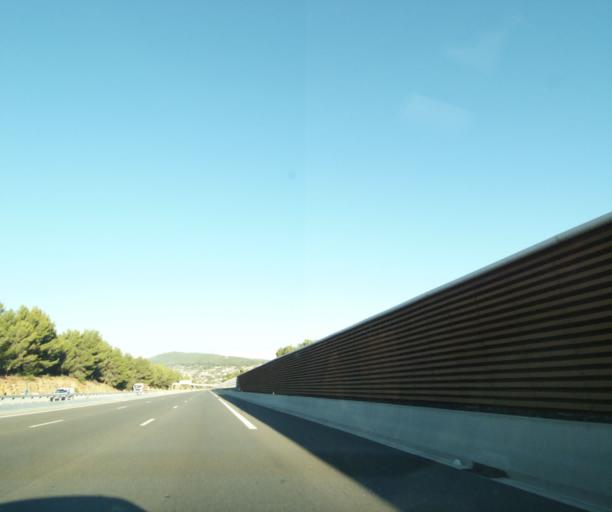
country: FR
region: Provence-Alpes-Cote d'Azur
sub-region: Departement des Bouches-du-Rhone
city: Ceyreste
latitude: 43.2064
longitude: 5.6126
